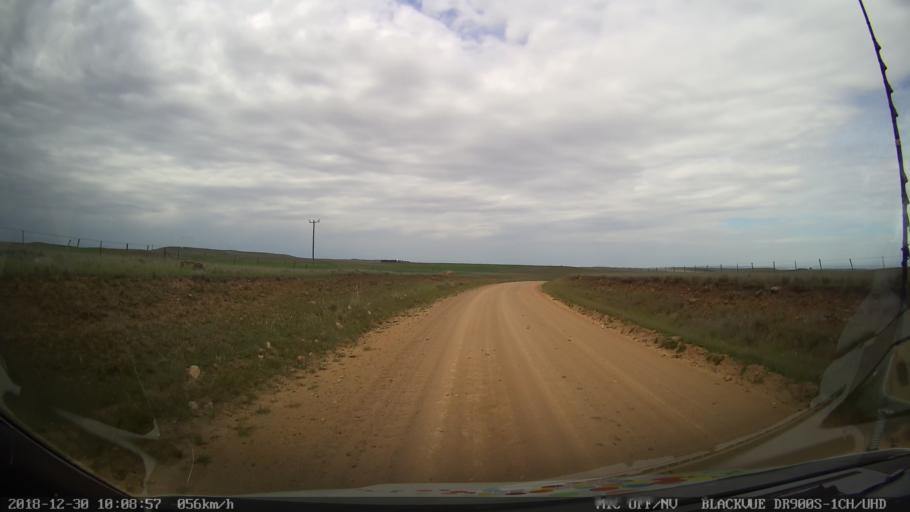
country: AU
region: New South Wales
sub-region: Cooma-Monaro
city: Cooma
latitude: -36.5467
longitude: 149.1093
